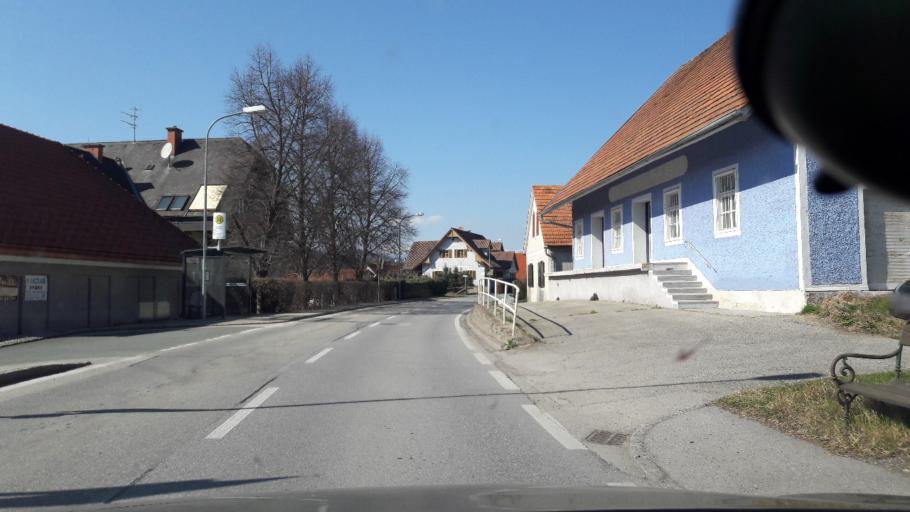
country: AT
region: Styria
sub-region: Politischer Bezirk Graz-Umgebung
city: Hitzendorf
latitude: 47.0358
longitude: 15.2992
